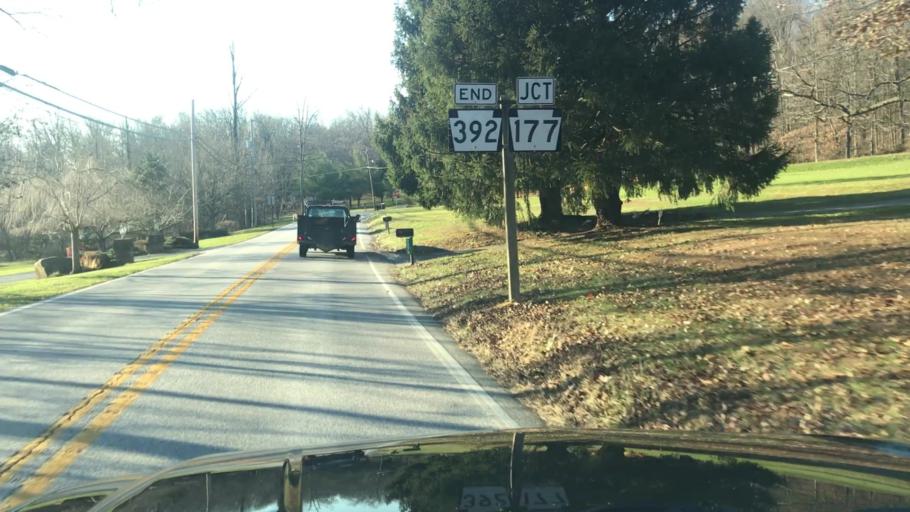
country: US
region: Pennsylvania
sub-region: York County
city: Valley Green
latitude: 40.1512
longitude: -76.8398
